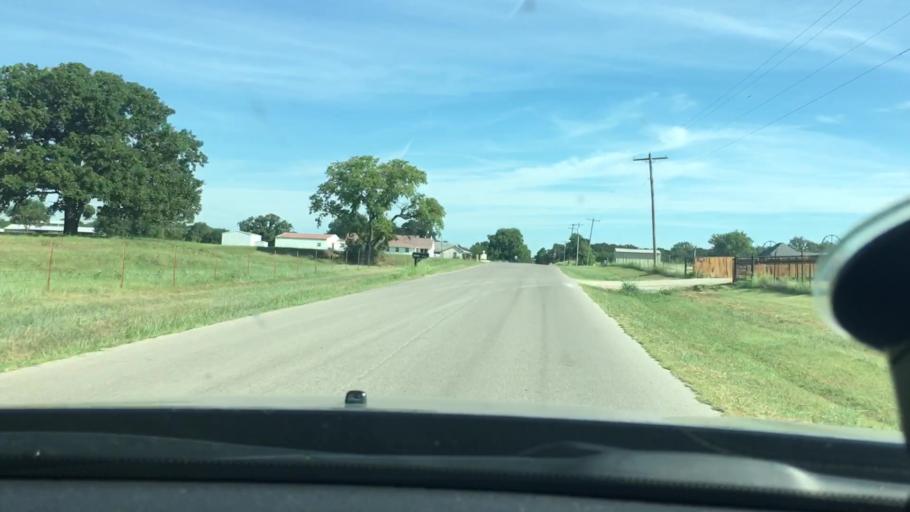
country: US
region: Oklahoma
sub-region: Carter County
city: Lone Grove
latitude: 34.2432
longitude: -97.2474
